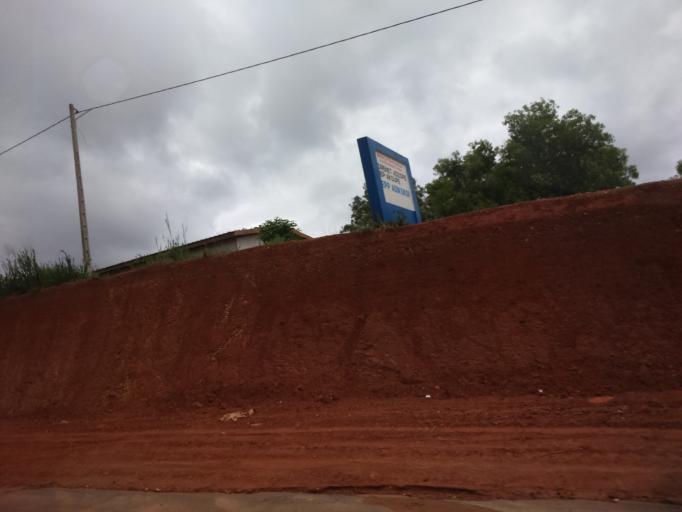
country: CI
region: Moyen-Comoe
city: Abengourou
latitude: 6.6281
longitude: -3.7107
